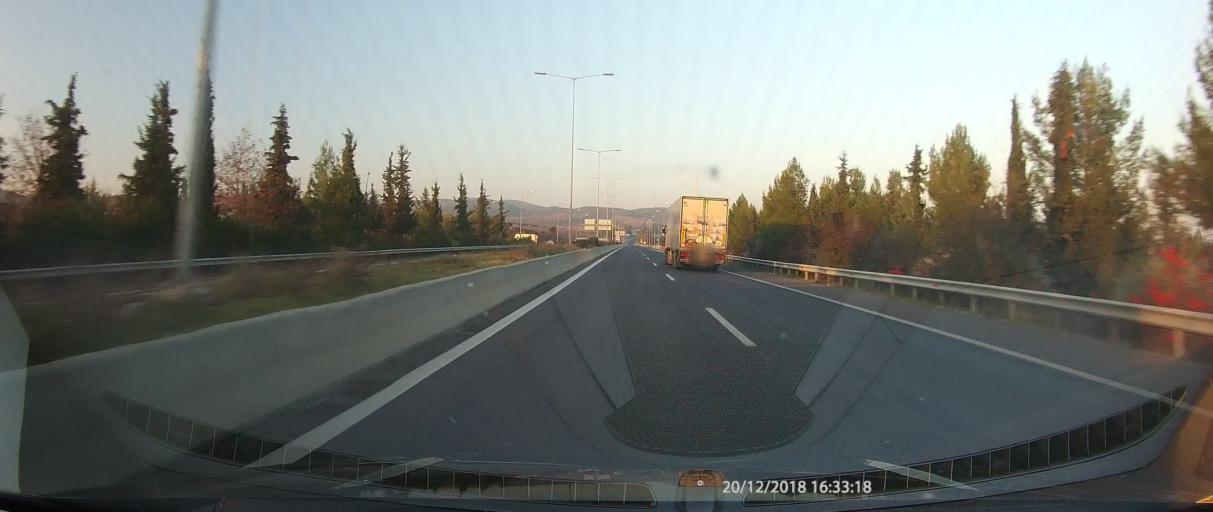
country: GR
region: Thessaly
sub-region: Nomos Magnisias
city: Evxinoupolis
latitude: 39.2615
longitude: 22.7370
